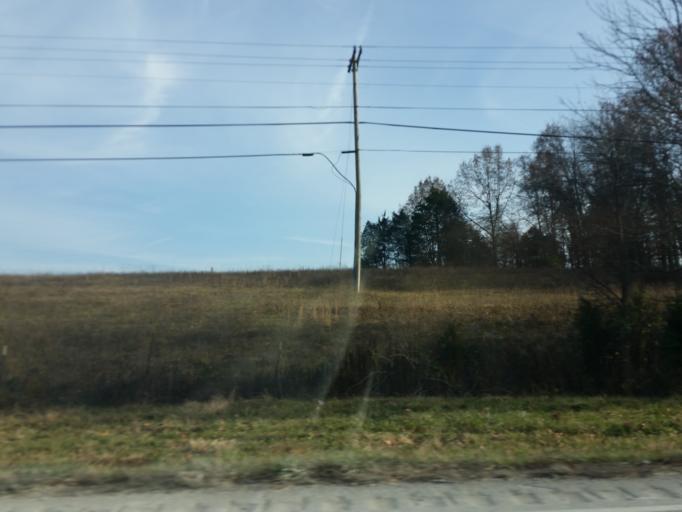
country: US
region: Kentucky
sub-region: Pendleton County
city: Falmouth
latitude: 38.7488
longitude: -84.3581
